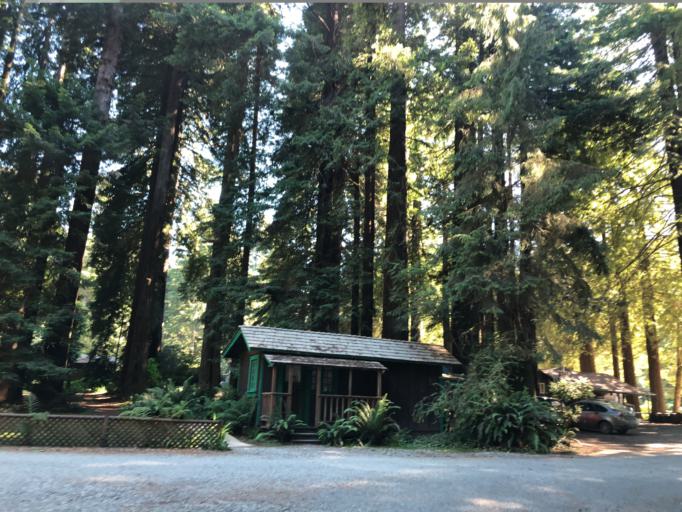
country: US
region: California
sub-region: Humboldt County
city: Westhaven-Moonstone
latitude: 41.0729
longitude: -124.1435
